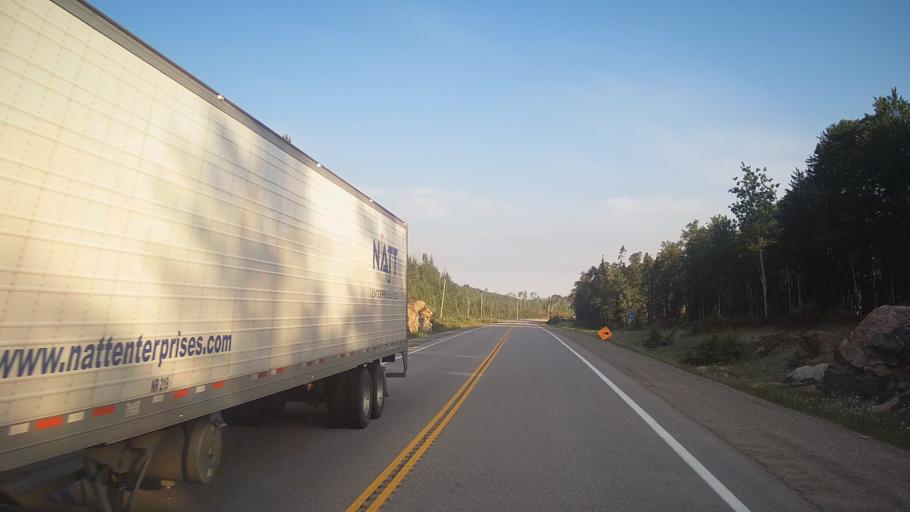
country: CA
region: Ontario
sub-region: Rainy River District
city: Atikokan
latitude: 49.3586
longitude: -91.5359
